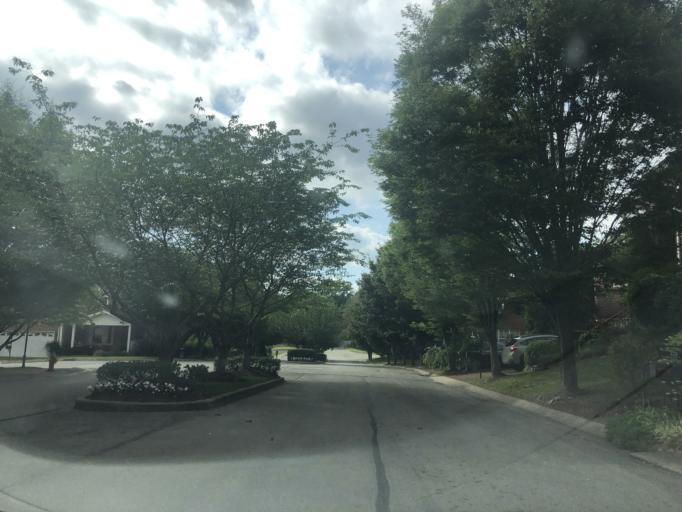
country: US
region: Tennessee
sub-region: Davidson County
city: Oak Hill
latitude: 36.0926
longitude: -86.8156
